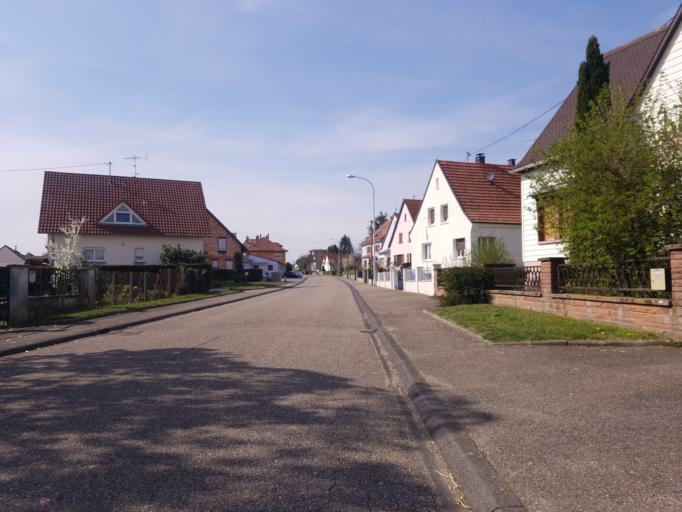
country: FR
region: Alsace
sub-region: Departement du Bas-Rhin
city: Soufflenheim
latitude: 48.8980
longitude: 7.9785
